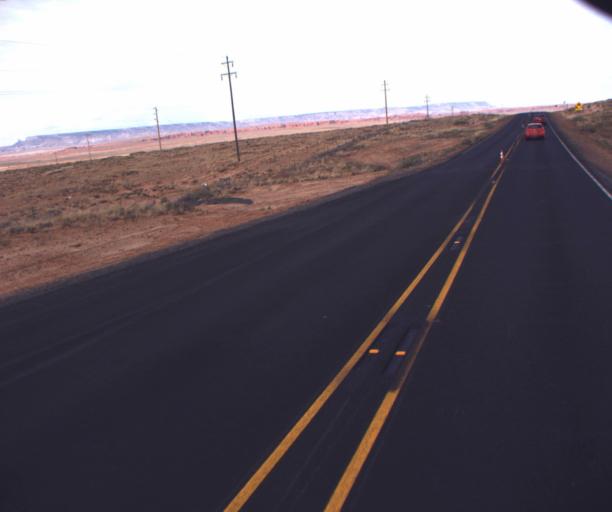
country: US
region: Arizona
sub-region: Apache County
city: Chinle
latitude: 36.0947
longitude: -109.6255
